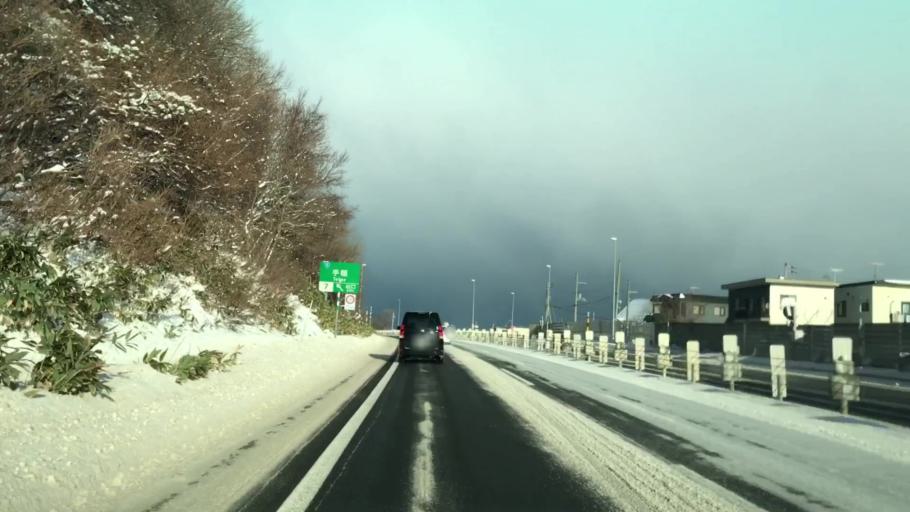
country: JP
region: Hokkaido
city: Sapporo
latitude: 43.1082
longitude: 141.2414
